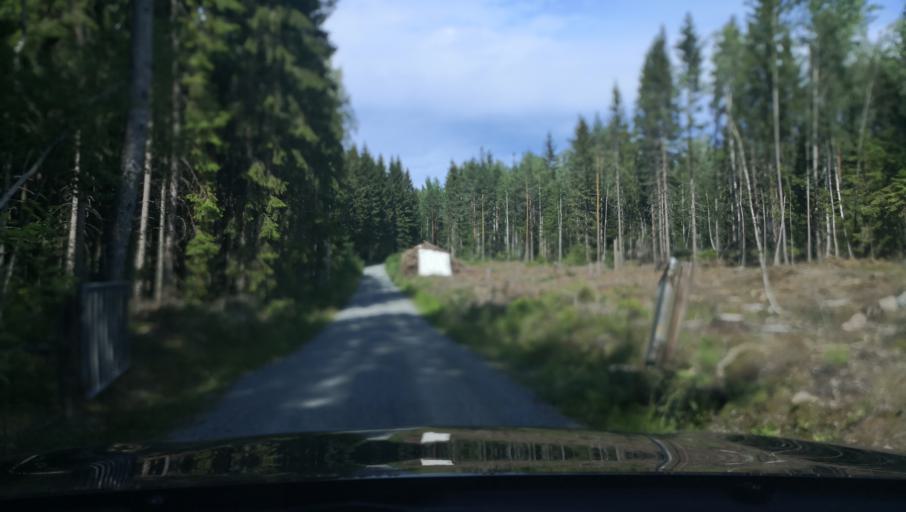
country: SE
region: Vaestmanland
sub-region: Surahammars Kommun
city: Ramnas
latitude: 59.9443
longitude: 16.1902
